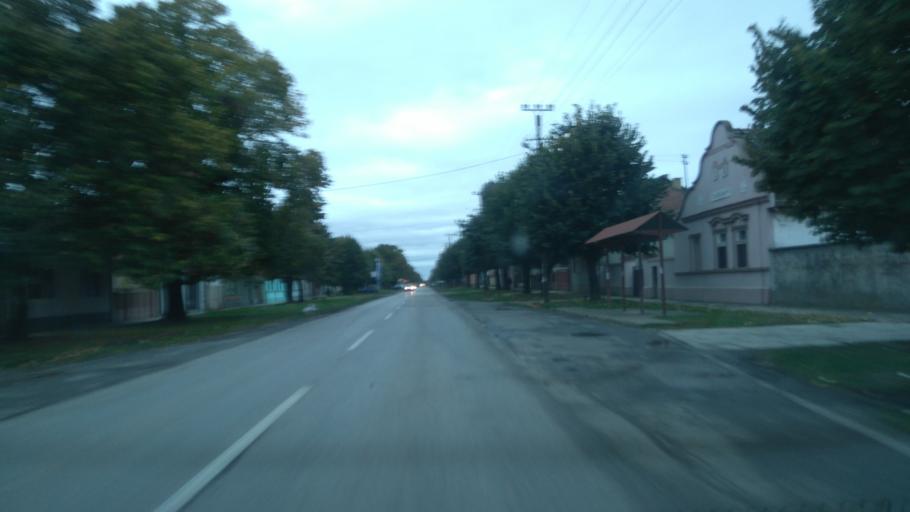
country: RS
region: Autonomna Pokrajina Vojvodina
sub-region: Juznobacki Okrug
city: Durdevo
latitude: 45.3300
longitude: 20.0632
